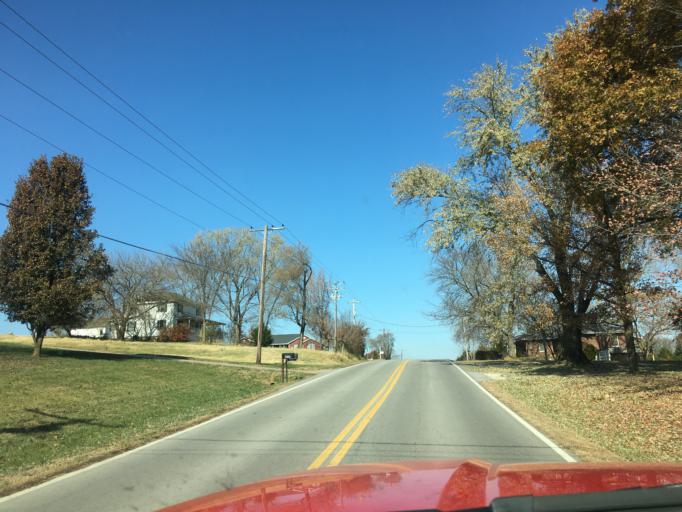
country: US
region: Missouri
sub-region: Cole County
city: Wardsville
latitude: 38.5093
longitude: -92.1757
